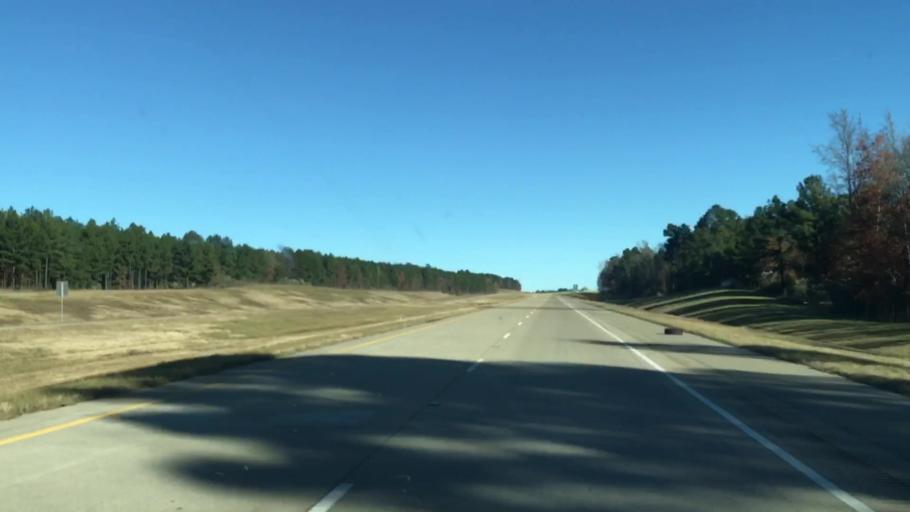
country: US
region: Louisiana
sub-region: Caddo Parish
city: Oil City
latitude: 32.8032
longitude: -93.8856
